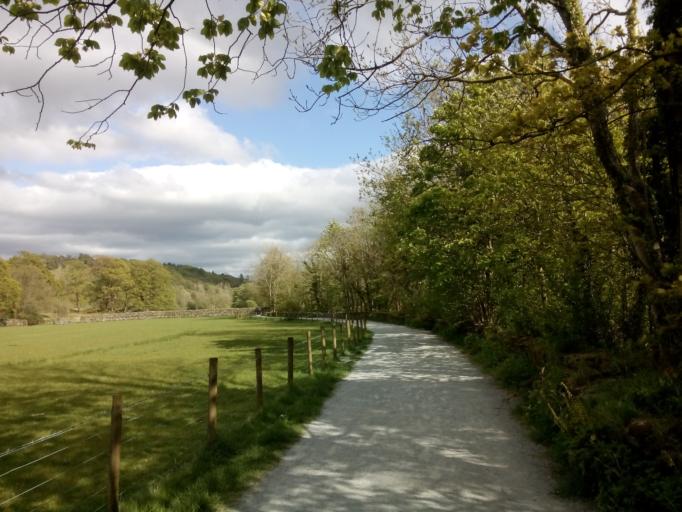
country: GB
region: England
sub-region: Cumbria
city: Ambleside
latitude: 54.4322
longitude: -3.0343
